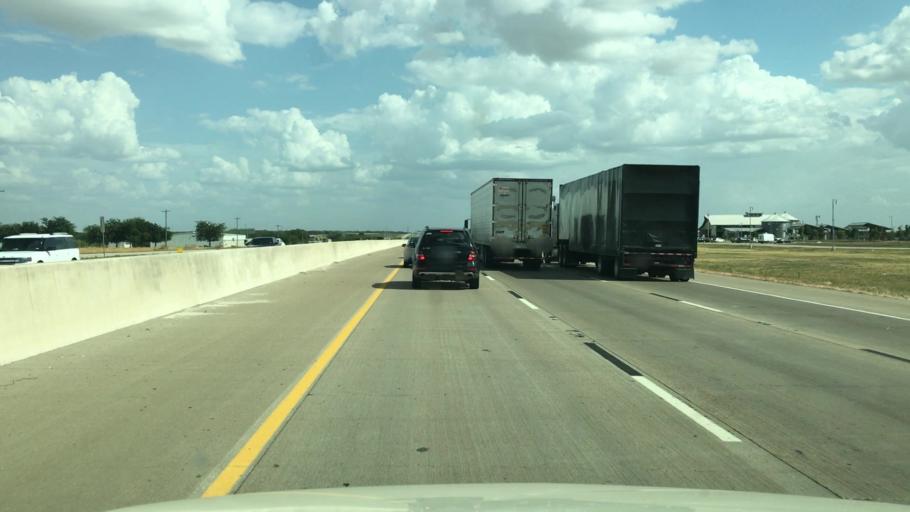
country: US
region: Texas
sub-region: Hill County
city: Hillsboro
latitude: 31.9292
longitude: -97.1033
